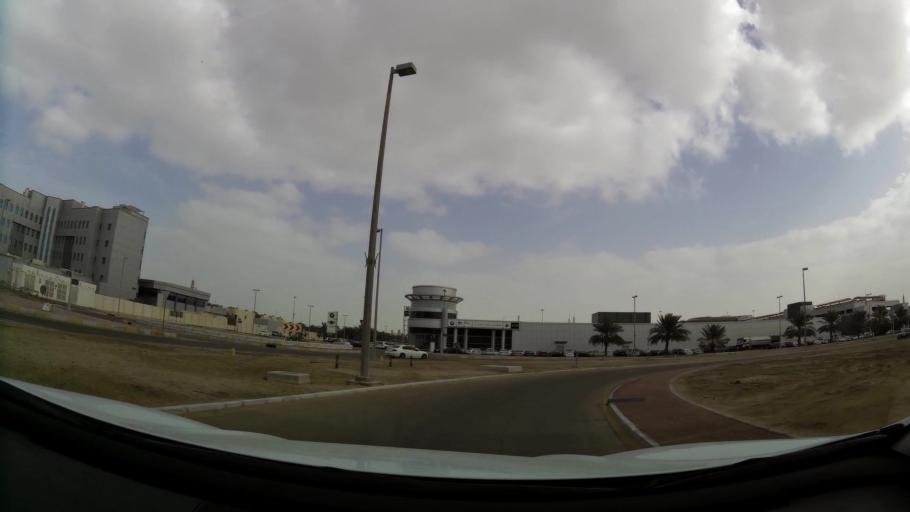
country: AE
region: Abu Dhabi
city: Abu Dhabi
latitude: 24.4161
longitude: 54.4931
